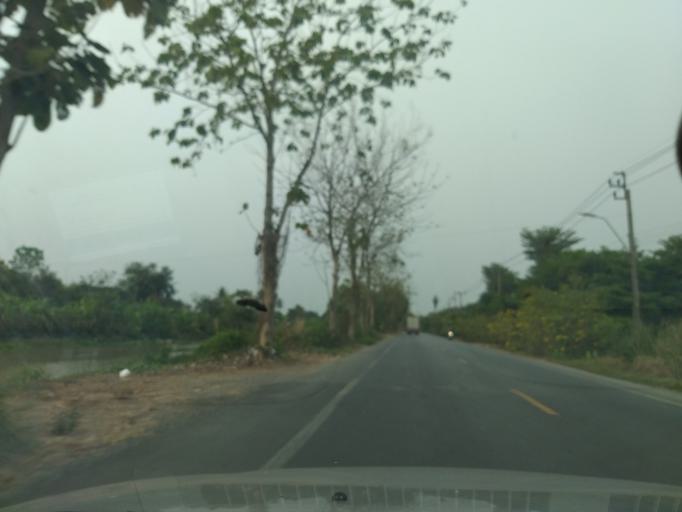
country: TH
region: Bangkok
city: Nong Chok
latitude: 13.9349
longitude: 100.8939
